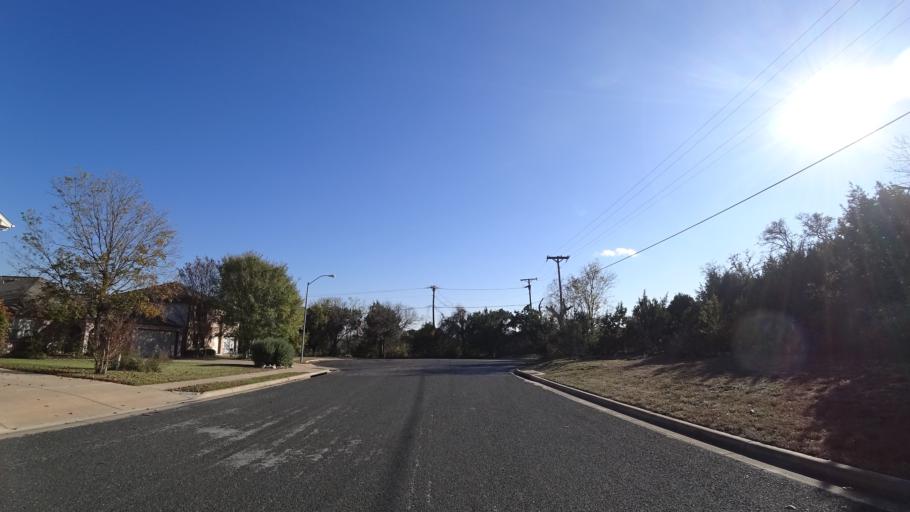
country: US
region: Texas
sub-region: Williamson County
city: Brushy Creek
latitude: 30.4850
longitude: -97.7430
